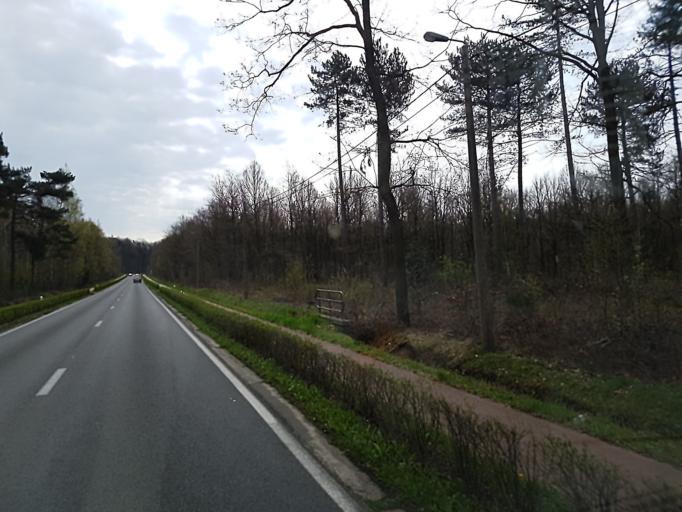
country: BE
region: Flanders
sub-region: Provincie Vlaams-Brabant
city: Scherpenheuvel-Zichem
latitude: 51.0394
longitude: 4.9667
